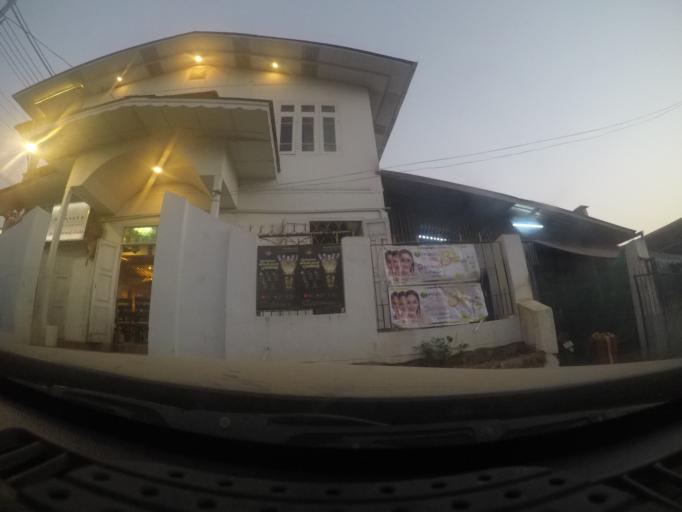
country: MM
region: Shan
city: Taunggyi
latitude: 20.7723
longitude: 97.0383
